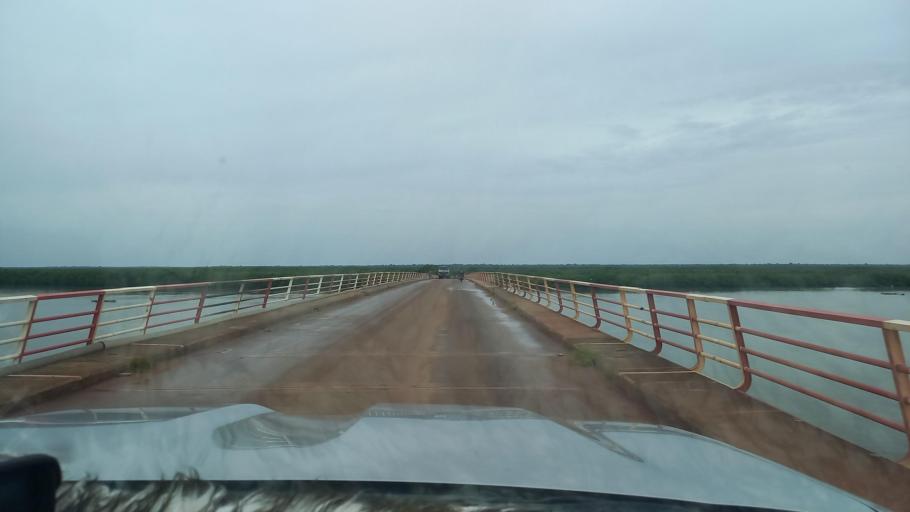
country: SN
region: Ziguinchor
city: Ziguinchor
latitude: 12.5894
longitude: -16.2628
